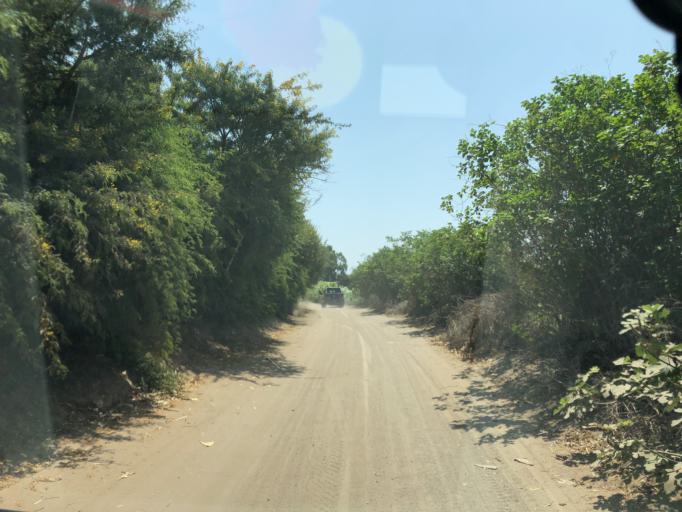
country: PE
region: Lima
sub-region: Provincia de Canete
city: San Vicente de Canete
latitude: -13.0104
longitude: -76.4645
